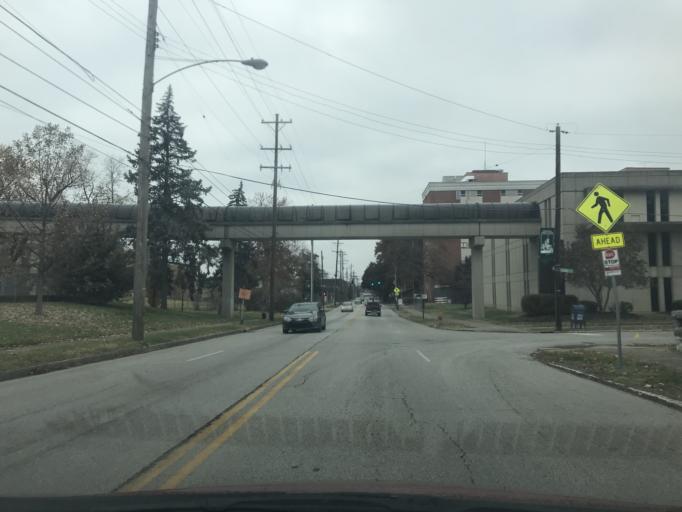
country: US
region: Kentucky
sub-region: Jefferson County
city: Louisville
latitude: 38.2411
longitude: -85.7318
